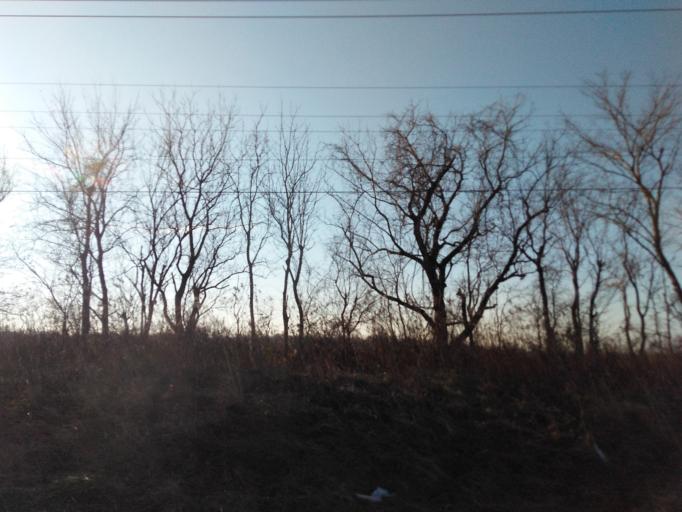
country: US
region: Illinois
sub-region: Madison County
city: Troy
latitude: 38.7175
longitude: -89.9001
